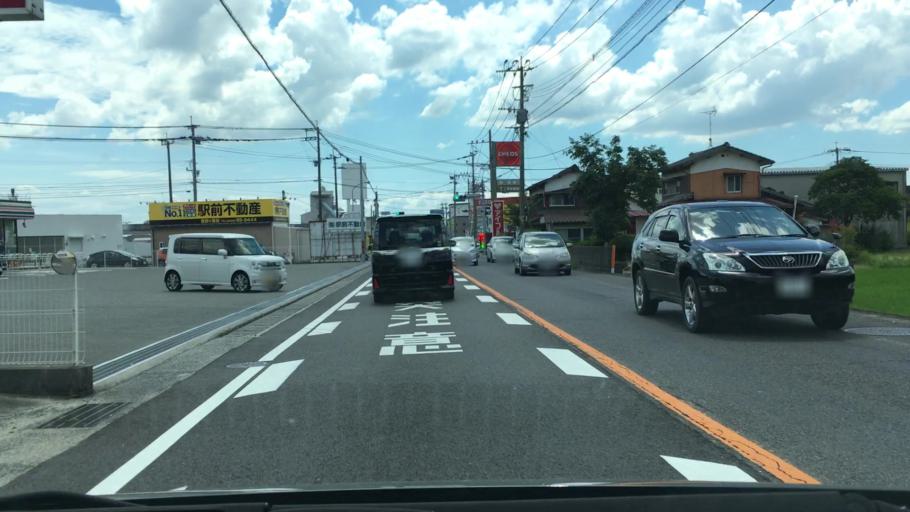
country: JP
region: Saga Prefecture
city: Kanzakimachi-kanzaki
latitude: 33.3331
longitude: 130.4146
